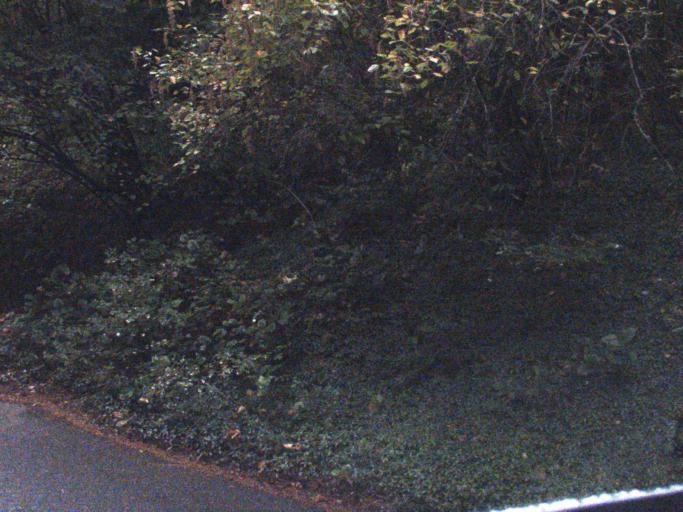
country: US
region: Washington
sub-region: Whatcom County
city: Bellingham
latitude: 48.6756
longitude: -122.4882
